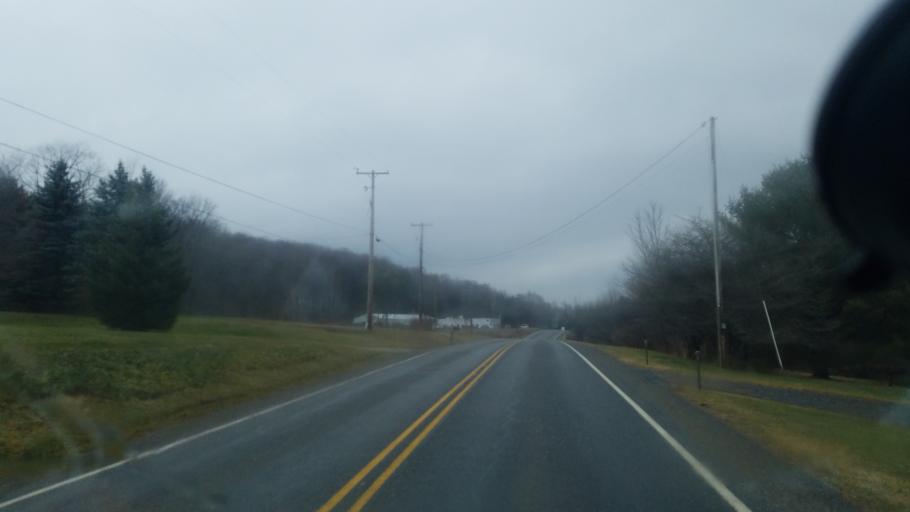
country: US
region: New York
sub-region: Allegany County
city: Wellsville
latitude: 41.9828
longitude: -77.8657
